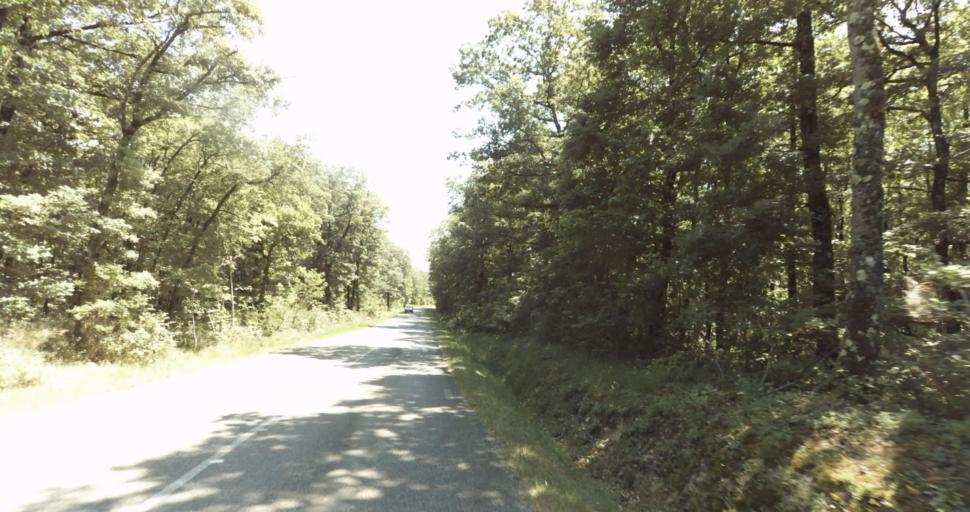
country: FR
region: Midi-Pyrenees
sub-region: Departement de la Haute-Garonne
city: Levignac
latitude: 43.6233
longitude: 1.1878
